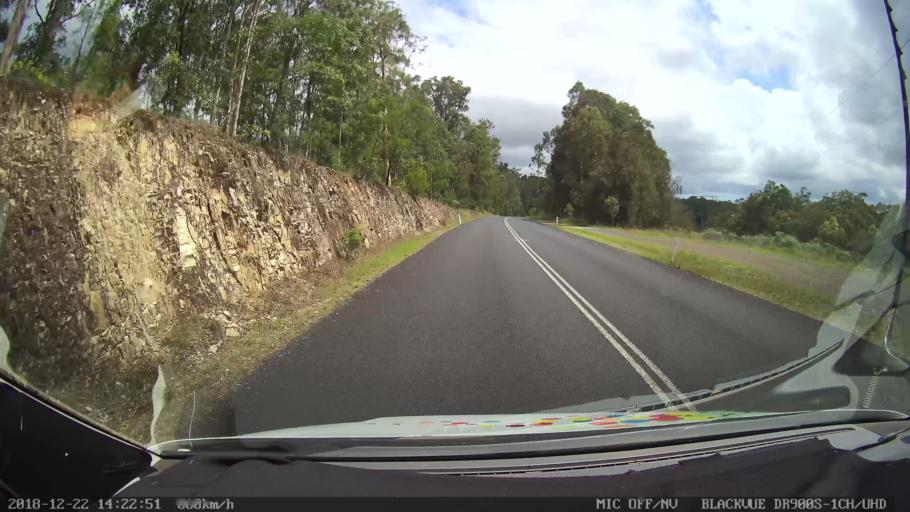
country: AU
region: New South Wales
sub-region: Clarence Valley
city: Coutts Crossing
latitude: -30.0294
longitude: 152.6535
